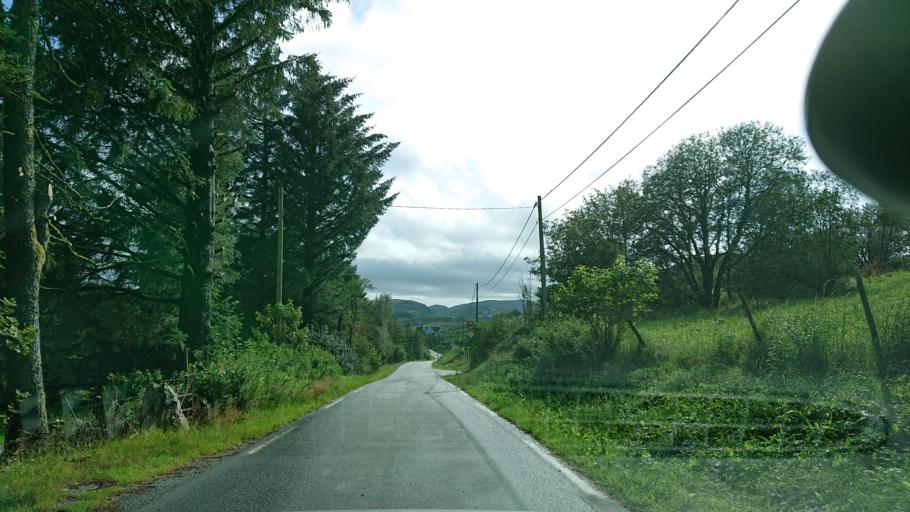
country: NO
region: Rogaland
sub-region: Gjesdal
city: Algard
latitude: 58.7011
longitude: 5.8906
